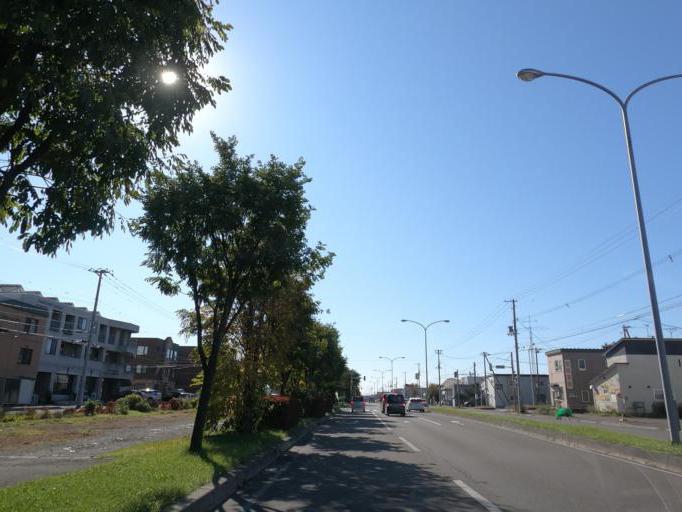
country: JP
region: Hokkaido
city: Obihiro
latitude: 42.9102
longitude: 143.2149
